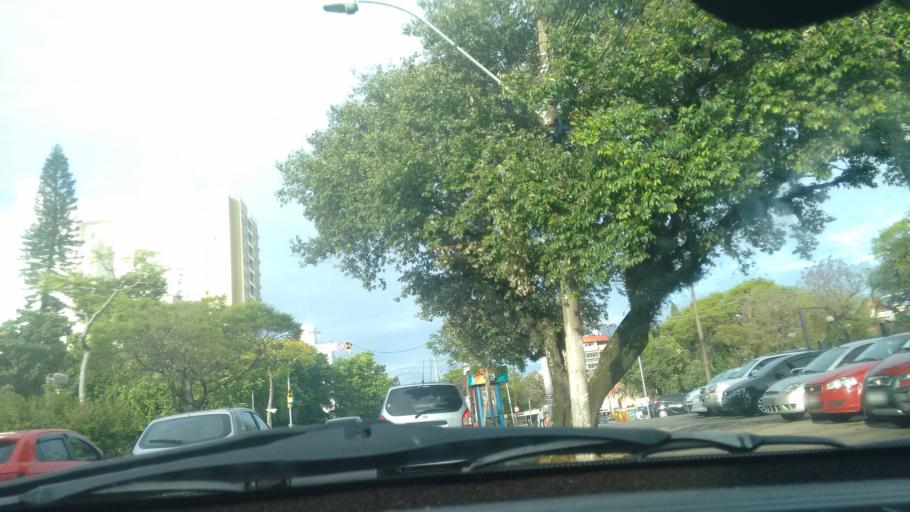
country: BR
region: Rio Grande do Sul
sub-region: Porto Alegre
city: Porto Alegre
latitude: -30.0206
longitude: -51.1809
